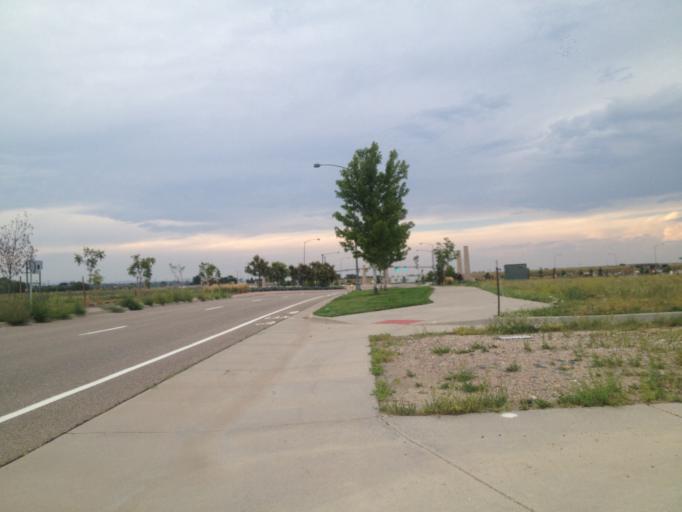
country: US
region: Colorado
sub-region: Boulder County
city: Louisville
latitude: 39.9445
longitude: -105.1232
